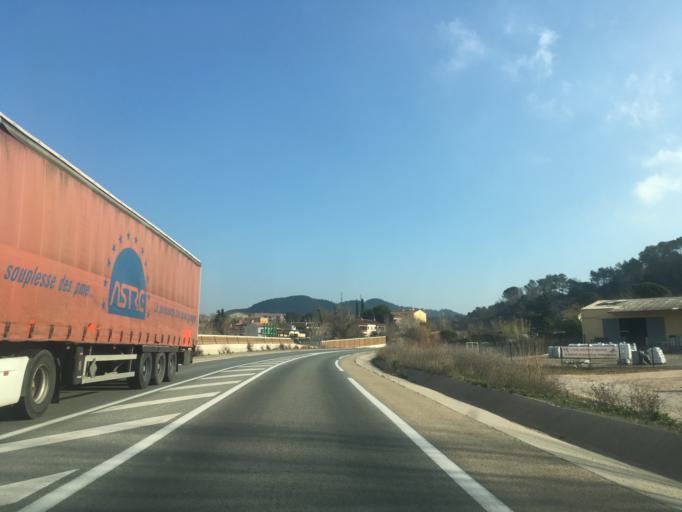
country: FR
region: Provence-Alpes-Cote d'Azur
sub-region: Departement du Var
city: Vidauban
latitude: 43.4229
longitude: 6.4279
